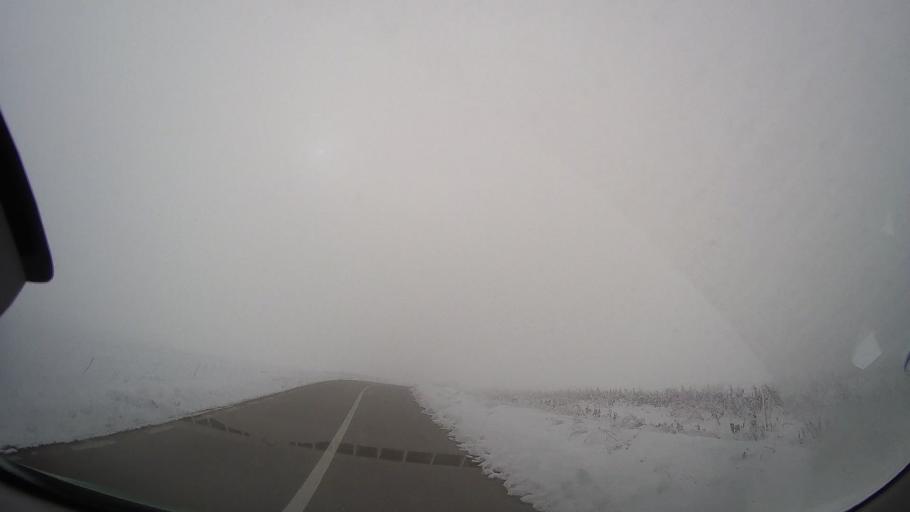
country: RO
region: Iasi
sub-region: Comuna Valea Seaca
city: Topile
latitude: 47.2723
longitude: 26.6704
